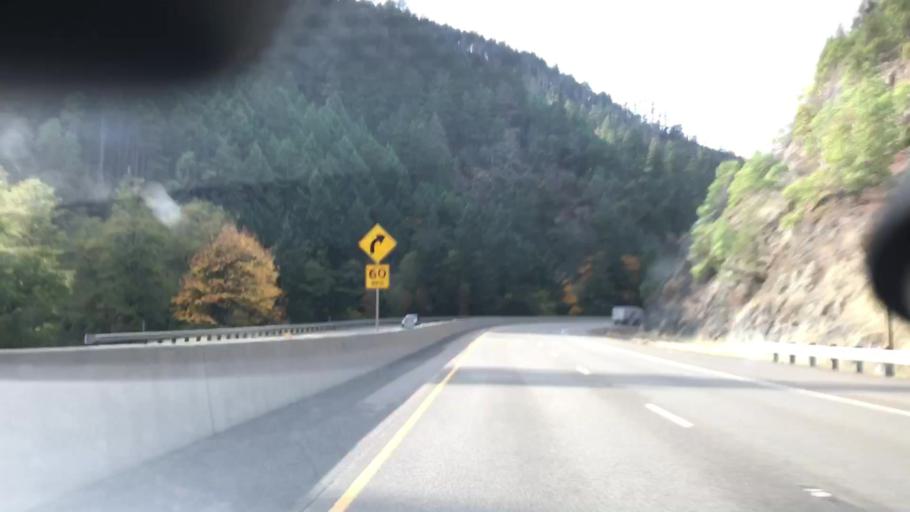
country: US
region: Oregon
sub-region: Douglas County
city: Canyonville
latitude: 42.9067
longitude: -123.2584
